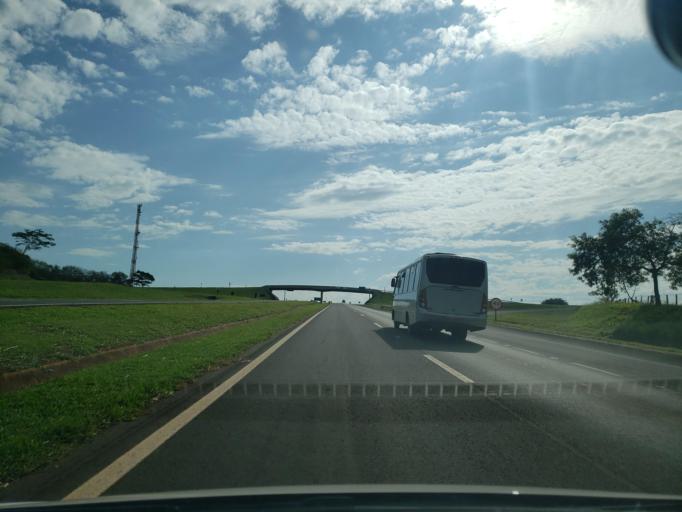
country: BR
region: Sao Paulo
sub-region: Promissao
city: Promissao
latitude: -21.6008
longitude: -49.8835
